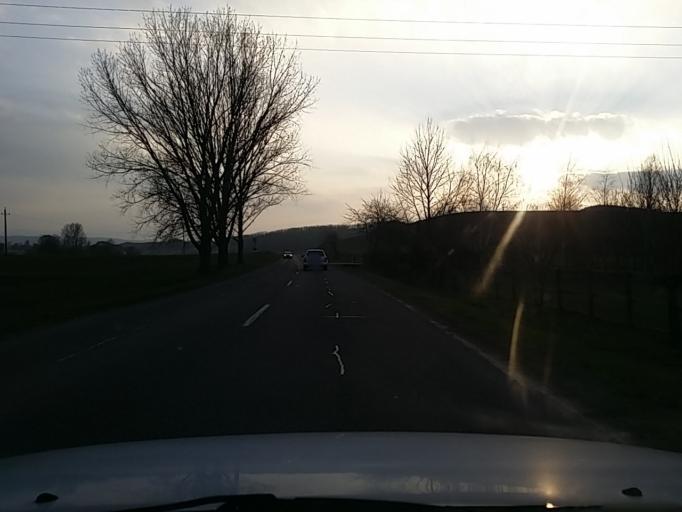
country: HU
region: Heves
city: Tarnalelesz
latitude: 48.0443
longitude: 20.1373
